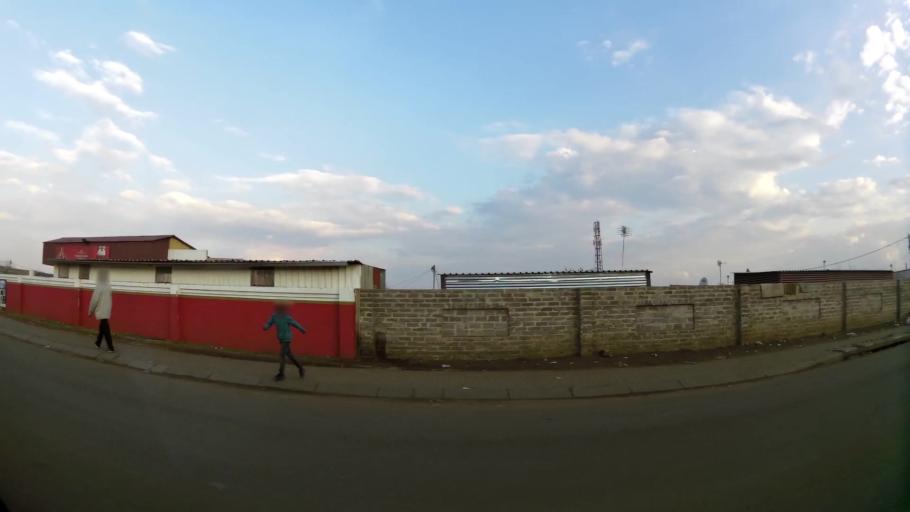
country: ZA
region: Gauteng
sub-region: City of Johannesburg Metropolitan Municipality
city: Orange Farm
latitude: -26.5368
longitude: 27.8344
